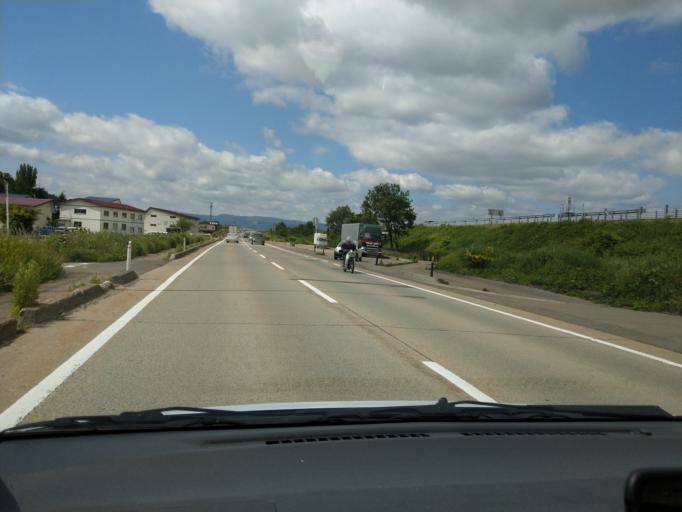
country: JP
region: Akita
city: Yuzawa
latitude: 39.2137
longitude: 140.5137
